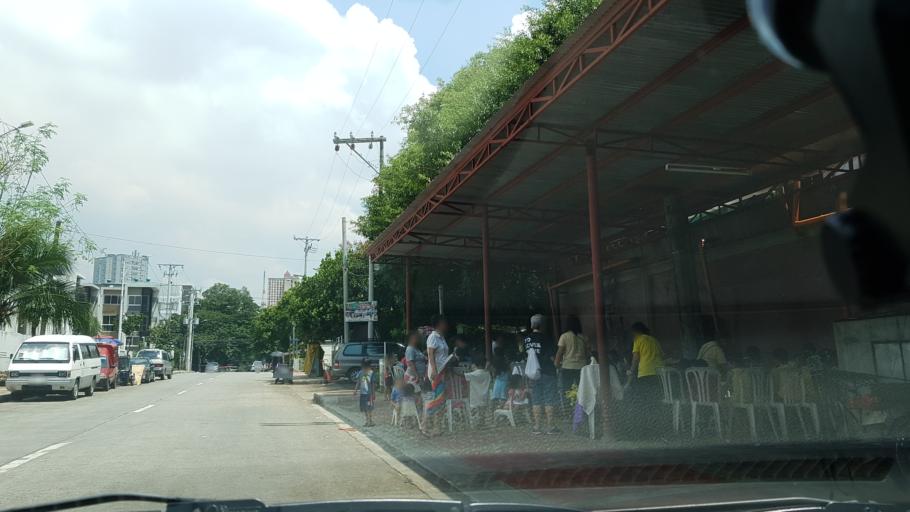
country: PH
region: Calabarzon
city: Del Monte
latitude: 14.6286
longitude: 121.0274
